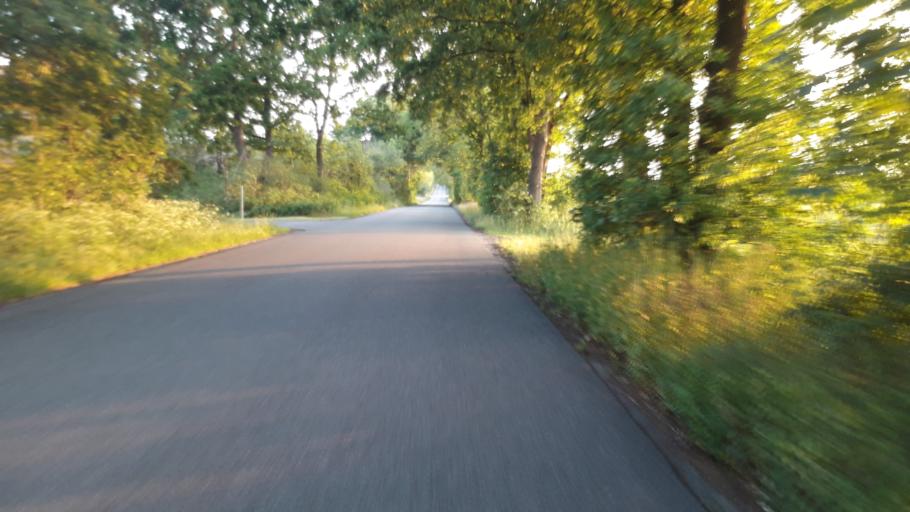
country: DE
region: North Rhine-Westphalia
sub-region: Regierungsbezirk Detmold
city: Hovelhof
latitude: 51.8646
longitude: 8.6681
